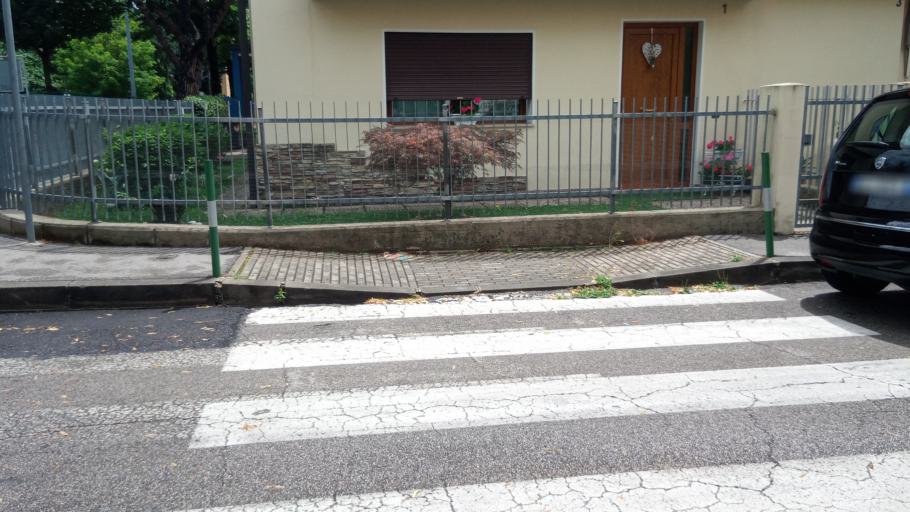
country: IT
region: Veneto
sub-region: Provincia di Padova
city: Padova
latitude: 45.4295
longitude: 11.8924
